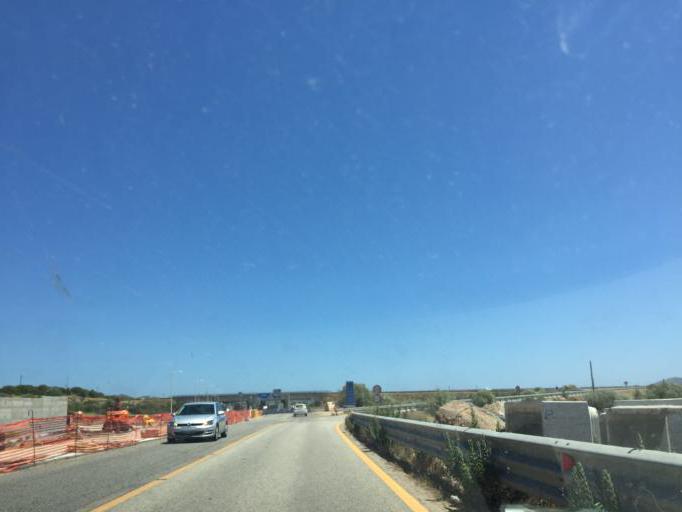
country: IT
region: Sardinia
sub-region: Provincia di Olbia-Tempio
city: Olbia
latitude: 40.8914
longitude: 9.4839
